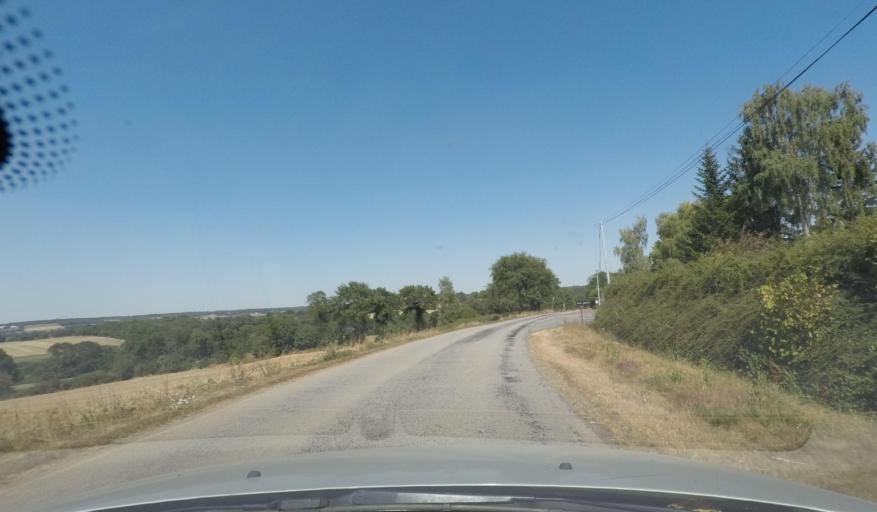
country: FR
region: Brittany
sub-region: Departement du Morbihan
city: Ruffiac
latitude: 47.8487
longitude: -2.2716
